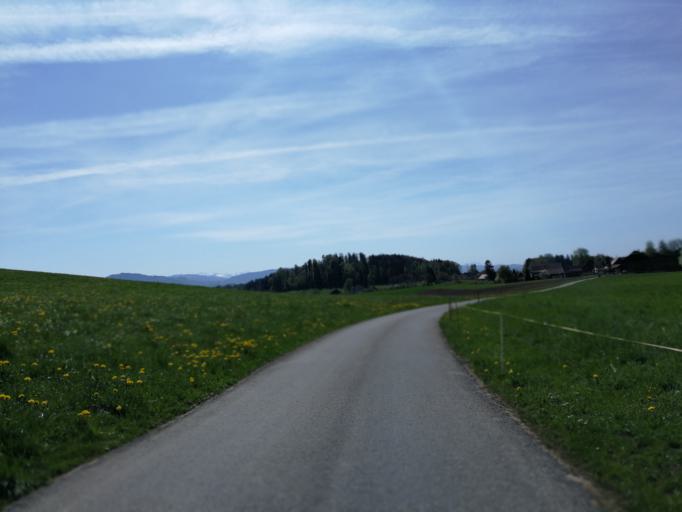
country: CH
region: Zurich
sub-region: Bezirk Hinwil
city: Bubikon
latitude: 47.2765
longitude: 8.8121
